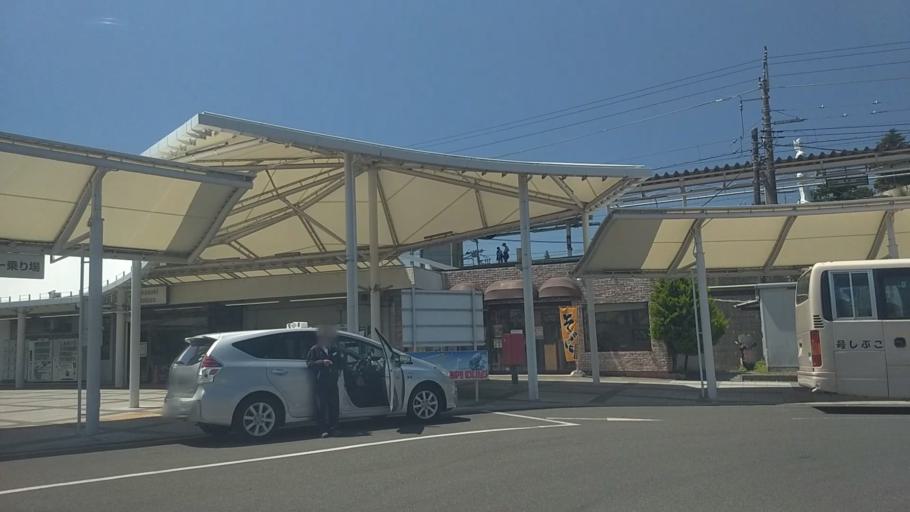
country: JP
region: Yamanashi
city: Nirasaki
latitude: 35.7108
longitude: 138.4509
